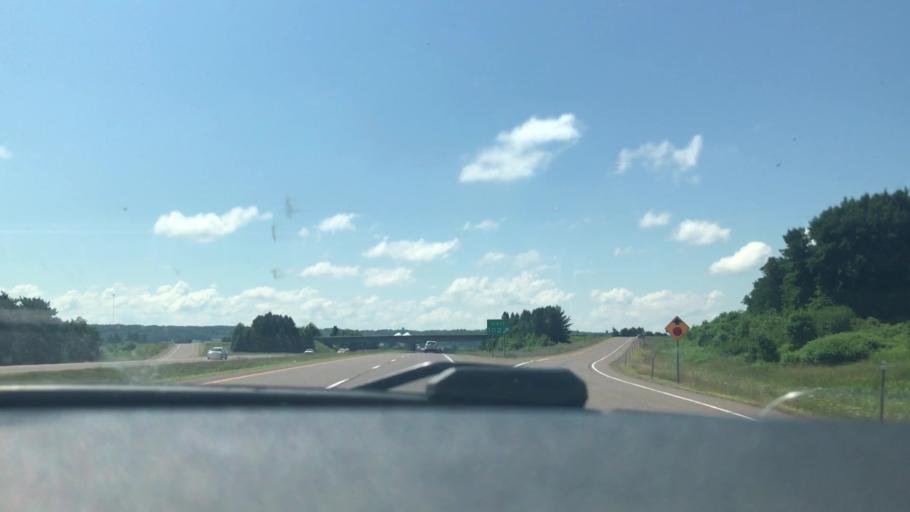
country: US
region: Wisconsin
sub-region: Chippewa County
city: Chippewa Falls
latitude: 45.0031
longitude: -91.4421
